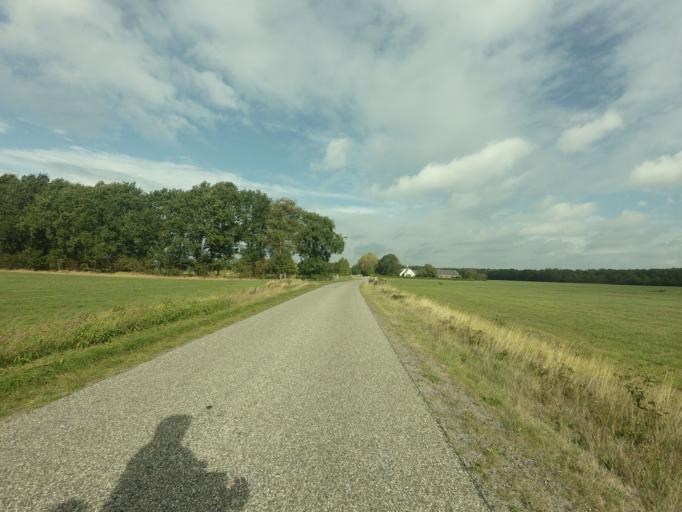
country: NL
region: Friesland
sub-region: Gemeente Heerenveen
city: Jubbega
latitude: 52.9813
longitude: 6.1192
